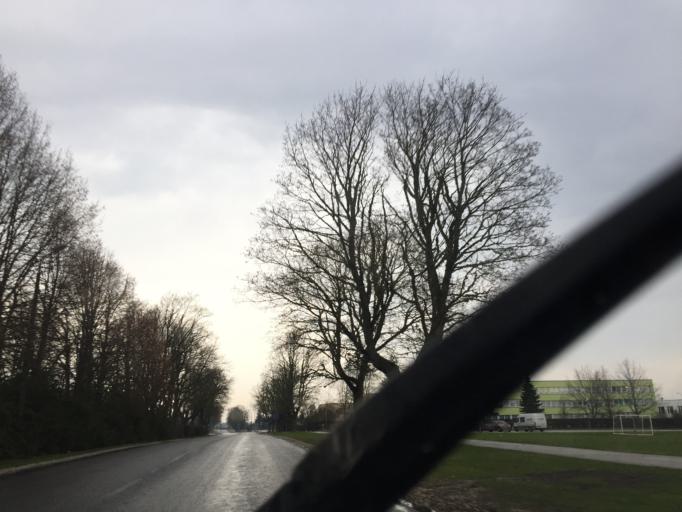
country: EE
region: Tartu
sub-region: UElenurme vald
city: Ulenurme
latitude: 58.3201
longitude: 26.7212
